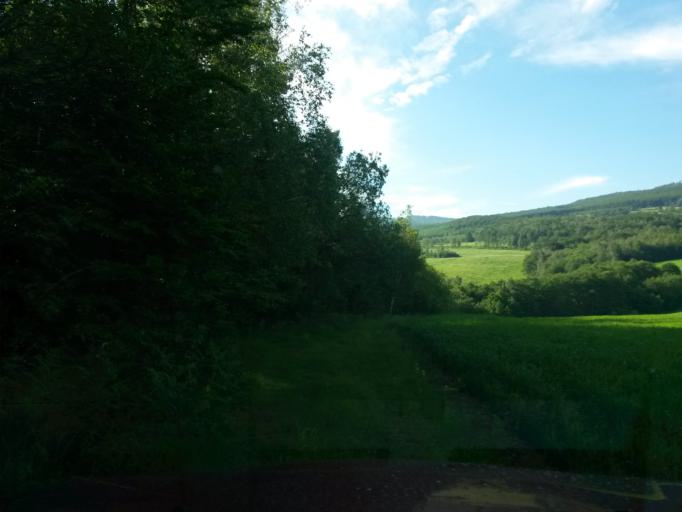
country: SK
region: Kosicky
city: Moldava nad Bodvou
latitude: 48.7289
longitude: 21.0820
